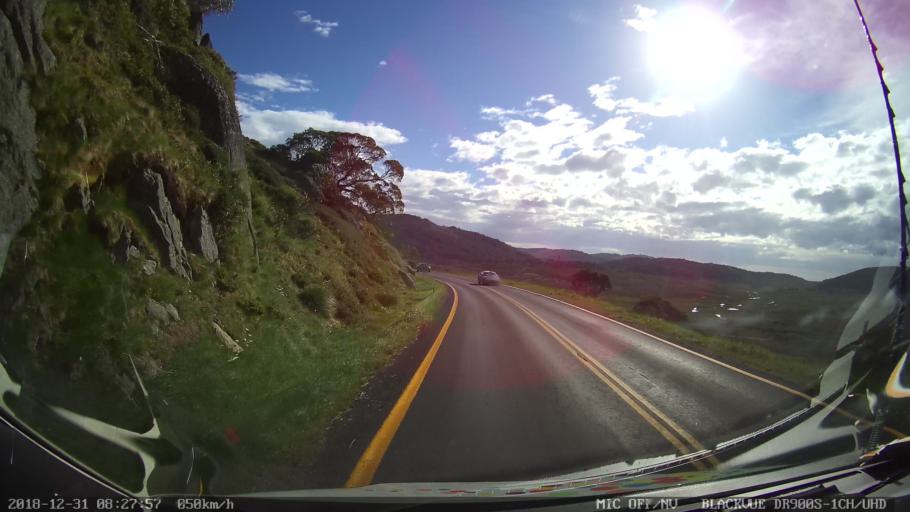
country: AU
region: New South Wales
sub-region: Snowy River
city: Jindabyne
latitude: -36.4302
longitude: 148.3423
